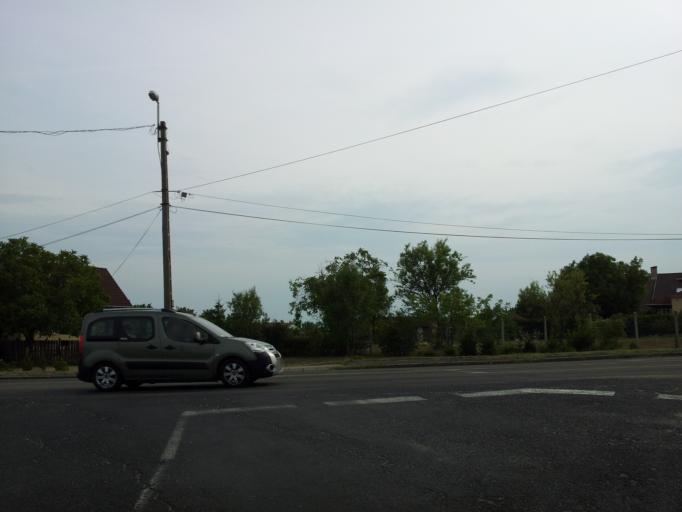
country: HU
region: Veszprem
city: Balatonfured
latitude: 46.9279
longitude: 17.8347
